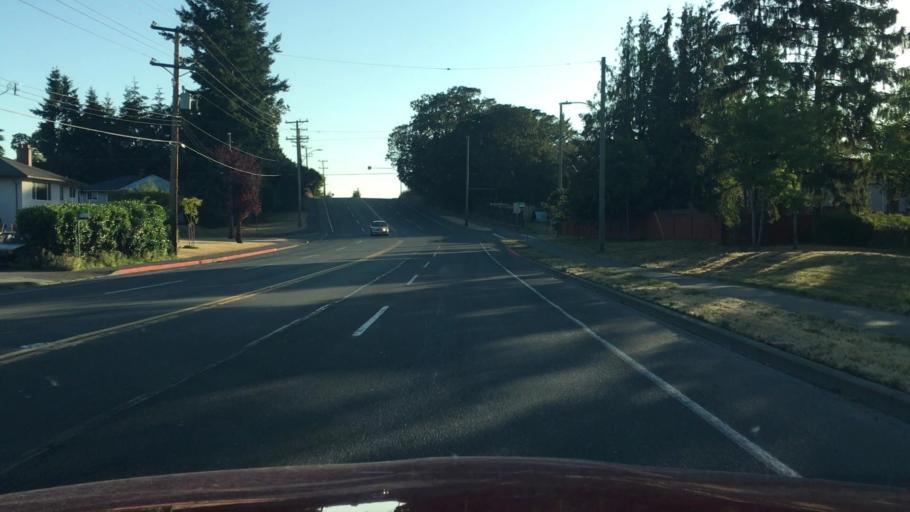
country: CA
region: British Columbia
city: Victoria
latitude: 48.4716
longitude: -123.3540
